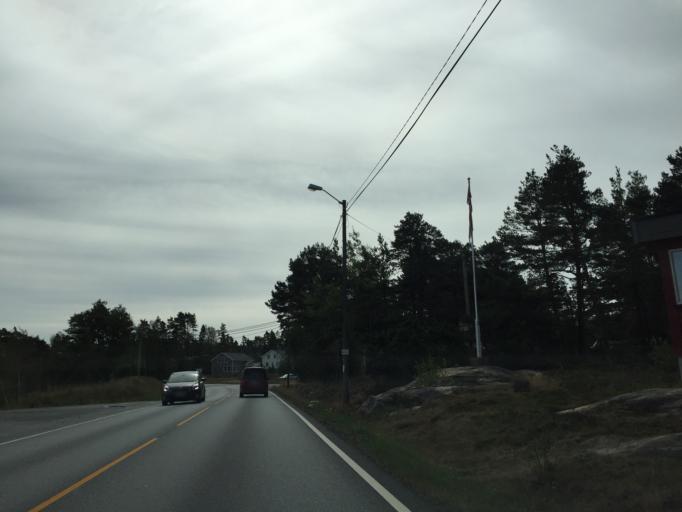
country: NO
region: Ostfold
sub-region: Fredrikstad
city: Fredrikstad
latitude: 59.1167
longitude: 10.9088
